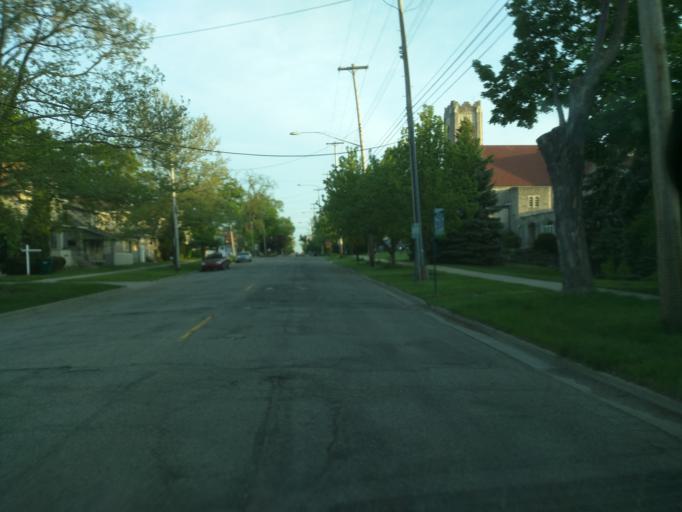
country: US
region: Michigan
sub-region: Ingham County
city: Lansing
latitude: 42.7458
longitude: -84.5538
